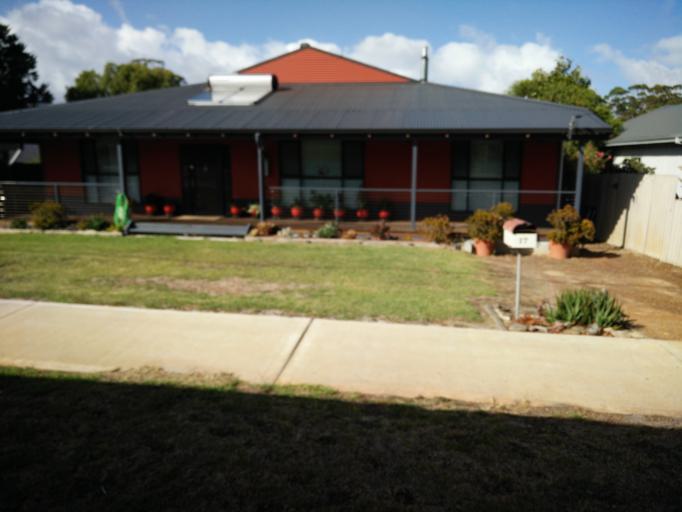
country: AU
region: Western Australia
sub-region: Manjimup
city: Manjimup
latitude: -34.2421
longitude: 116.1392
